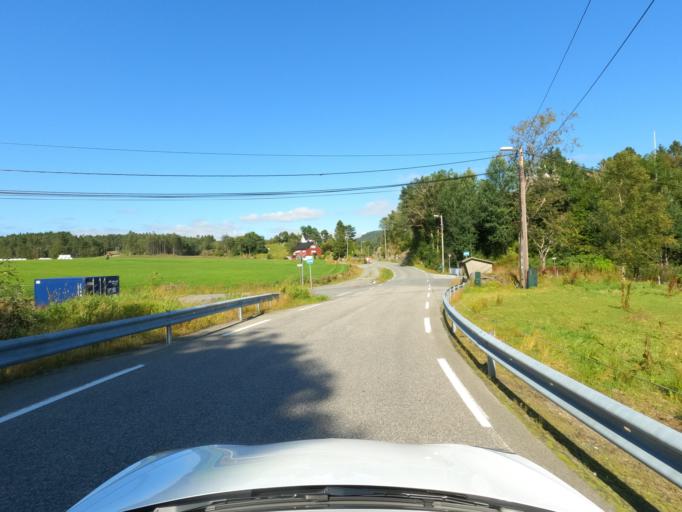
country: NO
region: Hordaland
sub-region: Bergen
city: Sandsli
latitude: 60.2649
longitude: 5.3124
